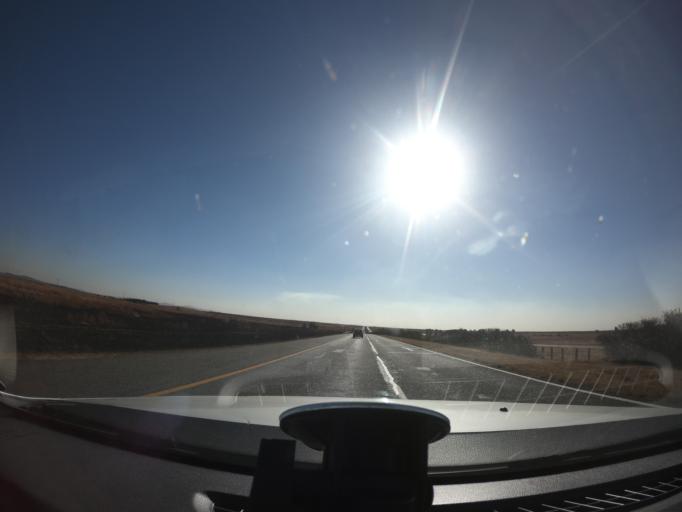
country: ZA
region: Gauteng
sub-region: Sedibeng District Municipality
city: Heidelberg
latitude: -26.4225
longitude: 28.2830
